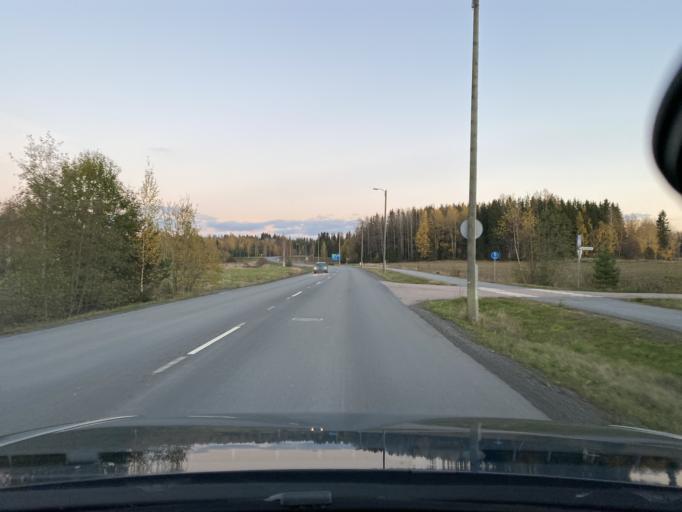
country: FI
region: Pirkanmaa
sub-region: Tampere
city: Lempaeaelae
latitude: 61.3279
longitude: 23.7675
